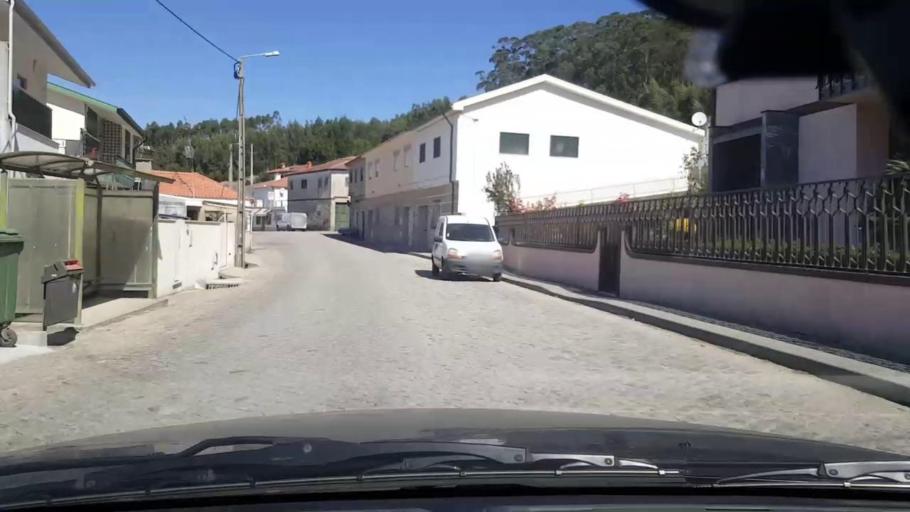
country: PT
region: Porto
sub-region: Maia
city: Gemunde
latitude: 41.3256
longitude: -8.6423
